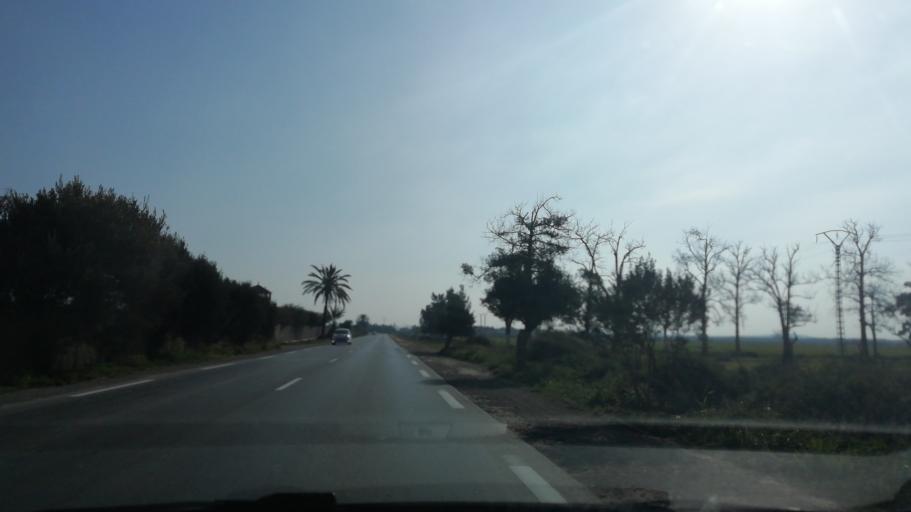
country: DZ
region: Mostaganem
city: Mostaganem
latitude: 35.7417
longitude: -0.0006
